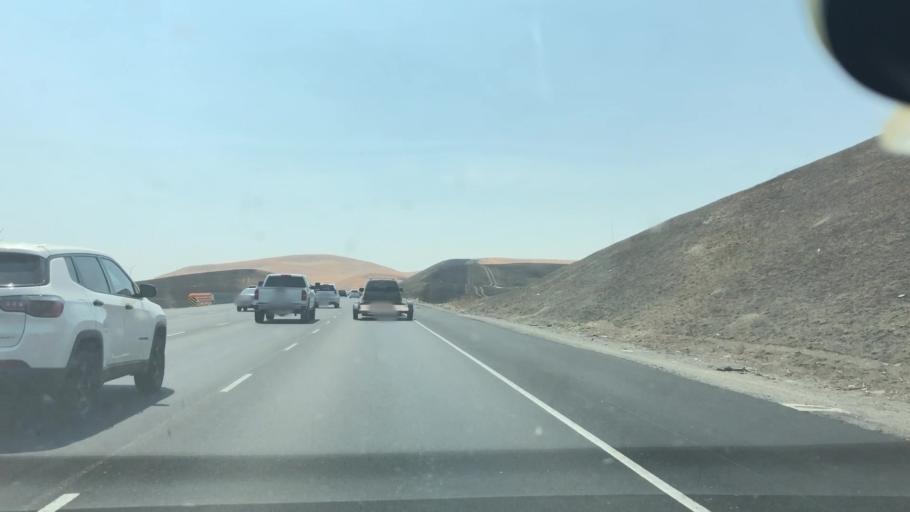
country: US
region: California
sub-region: San Joaquin County
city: Mountain House
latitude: 37.7354
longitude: -121.6190
